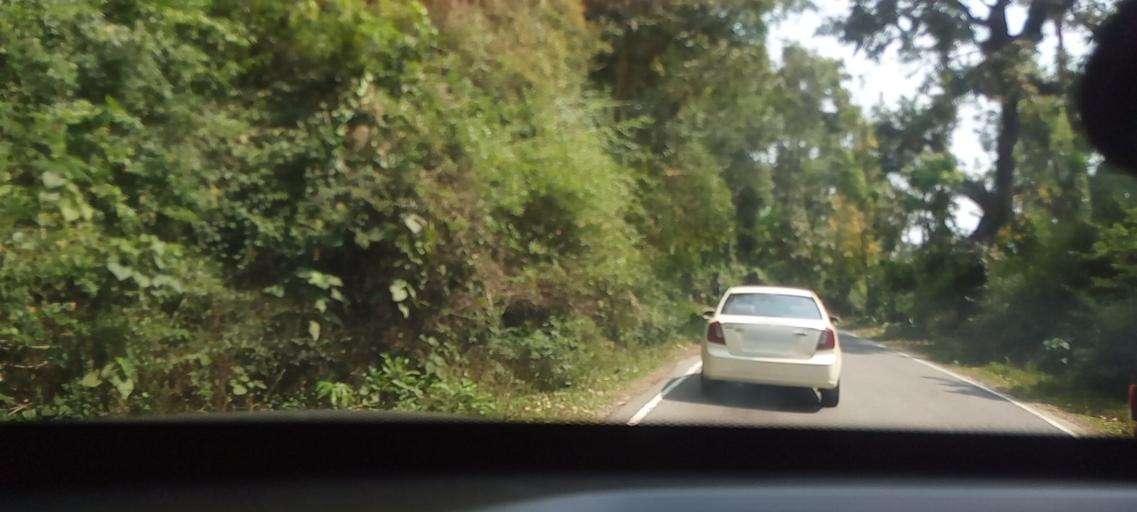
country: IN
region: Karnataka
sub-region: Chikmagalur
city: Mudigere
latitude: 13.2640
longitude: 75.6250
